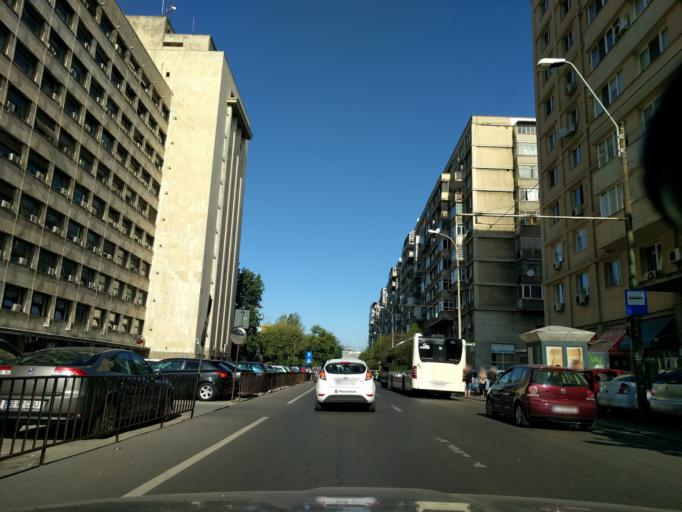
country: RO
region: Bucuresti
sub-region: Municipiul Bucuresti
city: Bucuresti
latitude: 44.4445
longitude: 26.0784
